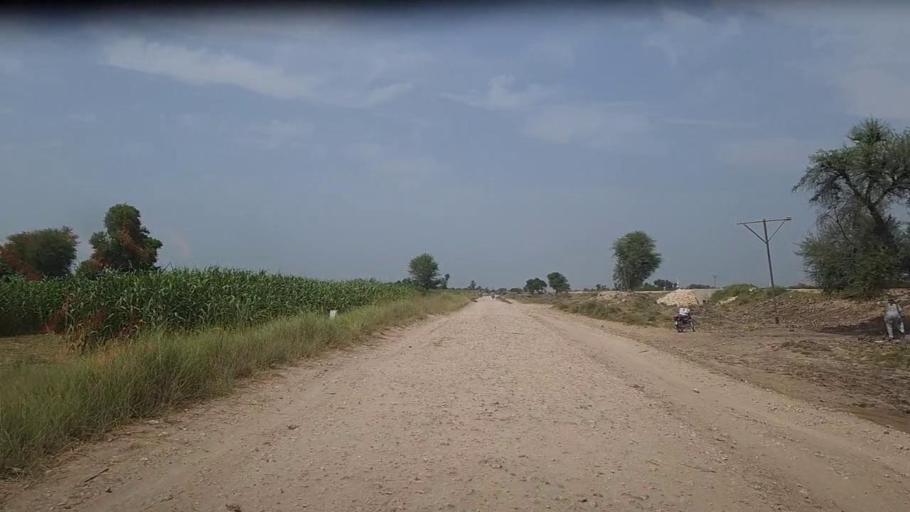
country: PK
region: Sindh
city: Bhiria
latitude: 26.9064
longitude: 68.2911
